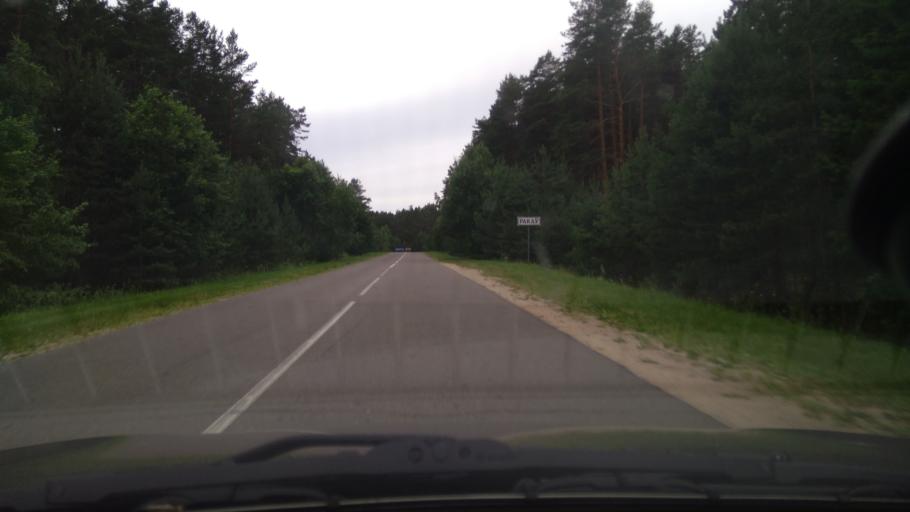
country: BY
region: Minsk
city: Rakaw
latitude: 53.9762
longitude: 27.0399
